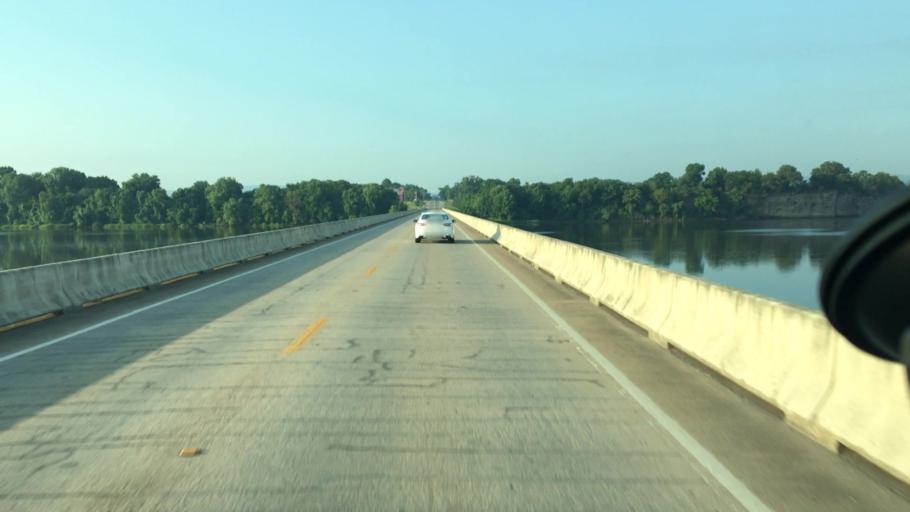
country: US
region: Arkansas
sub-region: Johnson County
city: Clarksville
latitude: 35.3950
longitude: -93.5306
